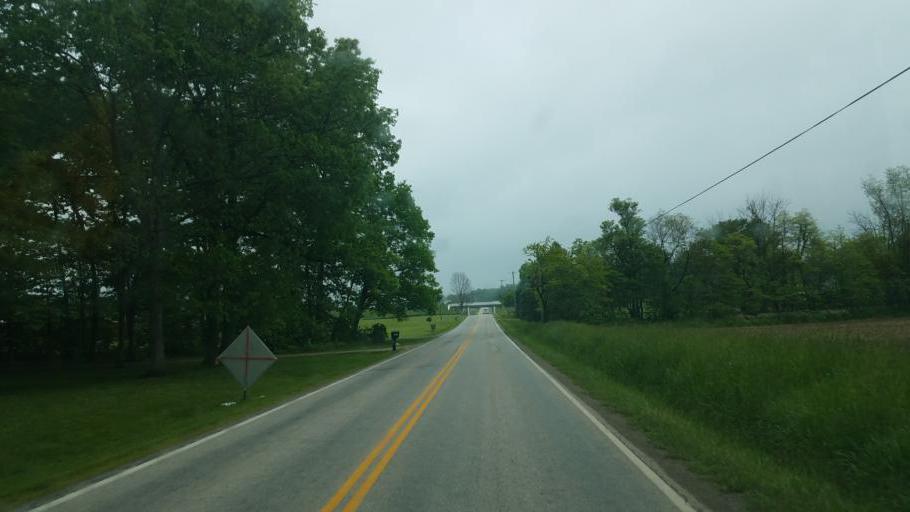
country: US
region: Ohio
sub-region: Ashland County
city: Ashland
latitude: 40.8196
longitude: -82.3364
